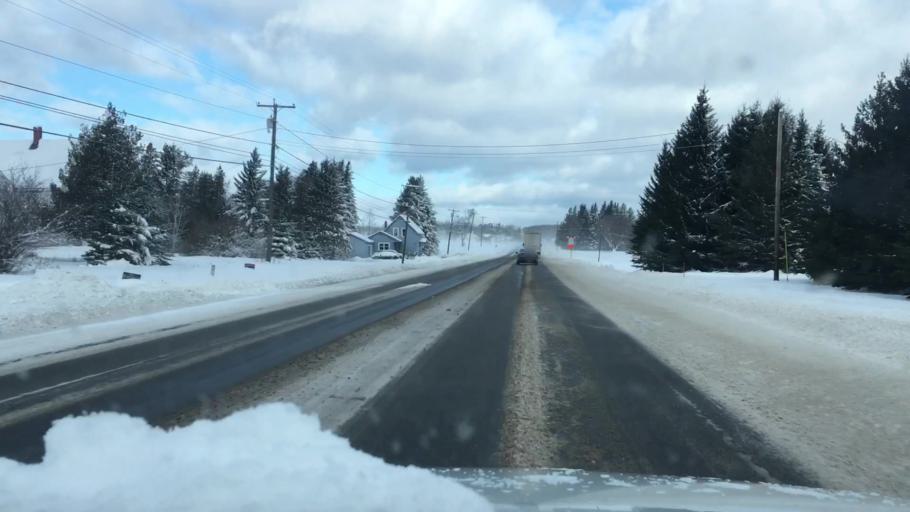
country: US
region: Maine
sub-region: Aroostook County
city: Caribou
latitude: 46.8055
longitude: -67.9935
